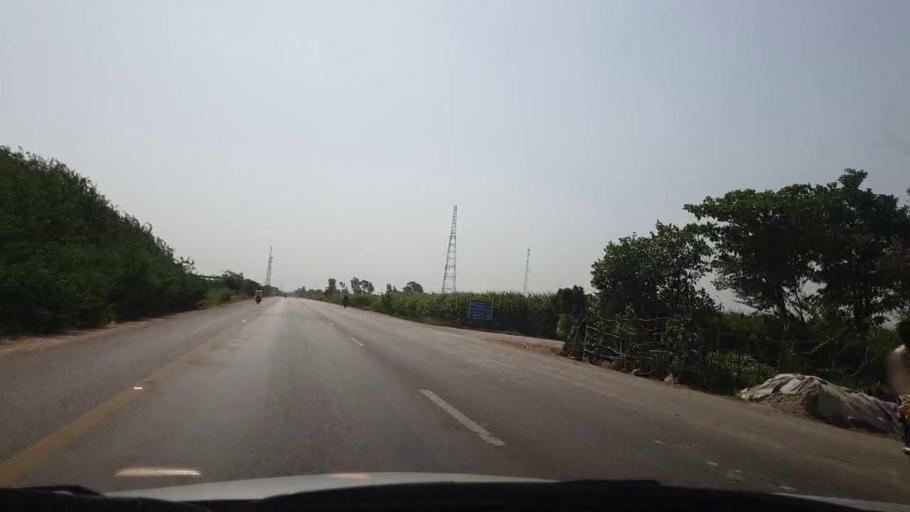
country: PK
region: Sindh
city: Tando Muhammad Khan
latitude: 25.0956
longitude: 68.5951
